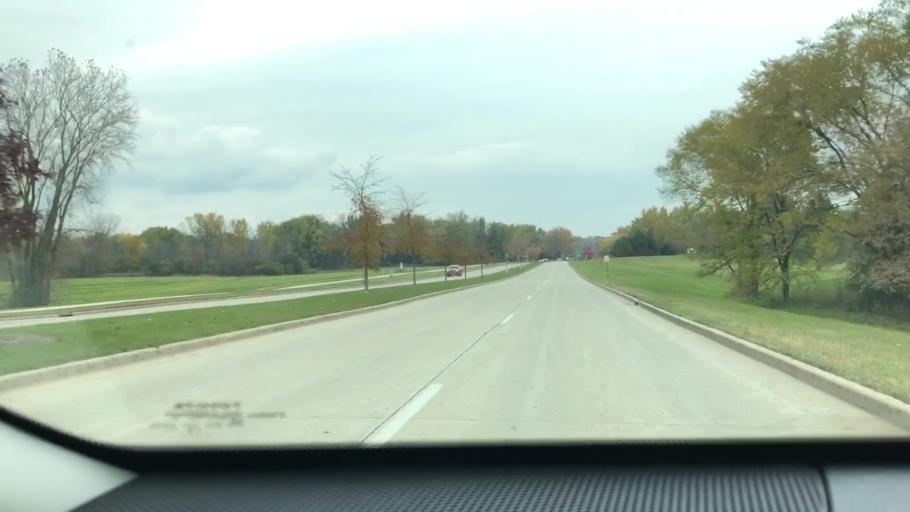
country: US
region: Wisconsin
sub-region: Brown County
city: Ashwaubenon
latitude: 44.4978
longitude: -88.1034
